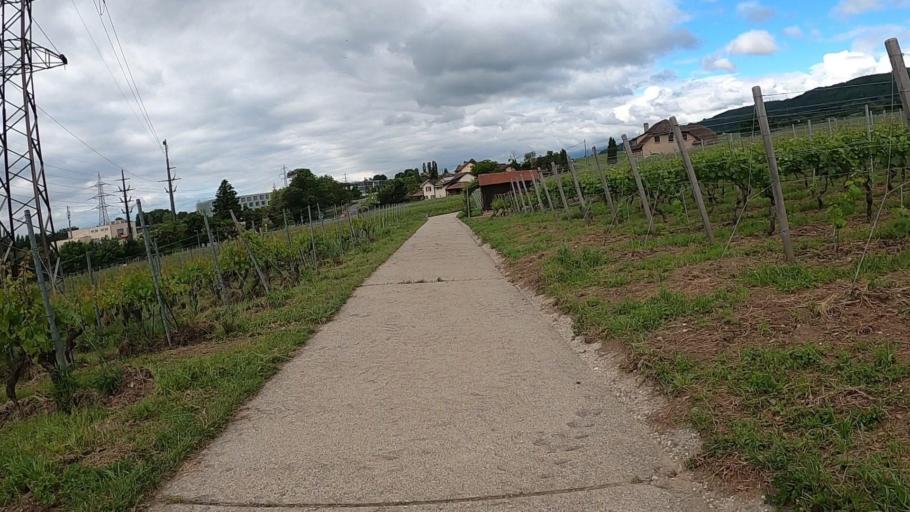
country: CH
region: Vaud
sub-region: Nyon District
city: Rolle
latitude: 46.4637
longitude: 6.3266
